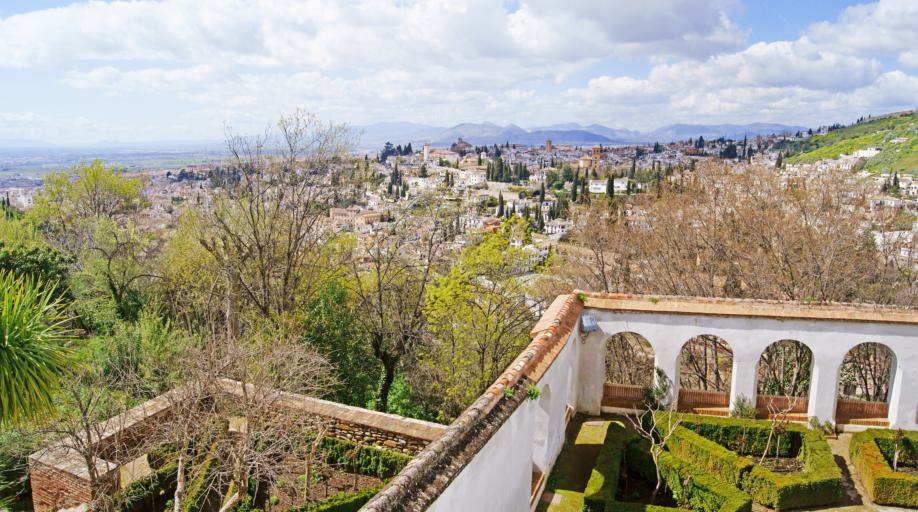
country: ES
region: Andalusia
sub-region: Provincia de Granada
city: Granada
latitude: 37.1784
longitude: -3.5857
